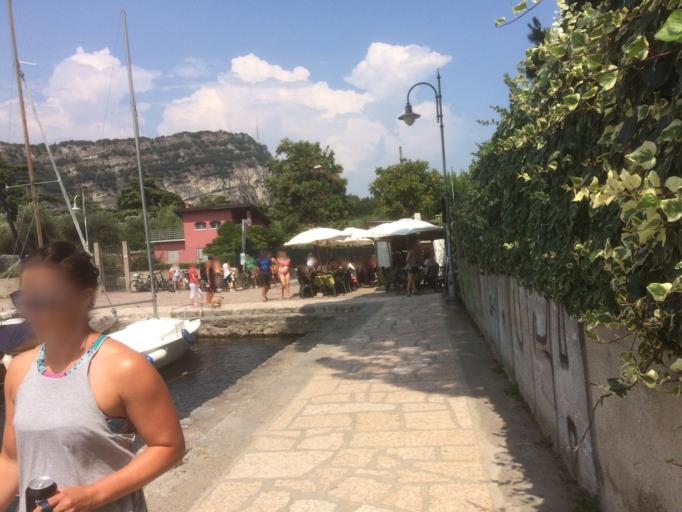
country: IT
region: Trentino-Alto Adige
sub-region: Provincia di Trento
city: Torbole sul Garda
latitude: 45.8708
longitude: 10.8721
